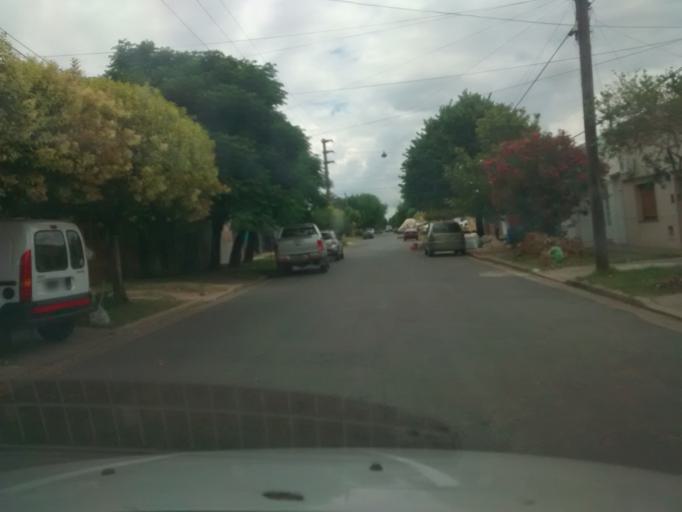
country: AR
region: Buenos Aires
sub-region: Partido de La Plata
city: La Plata
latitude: -34.9246
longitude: -57.9167
